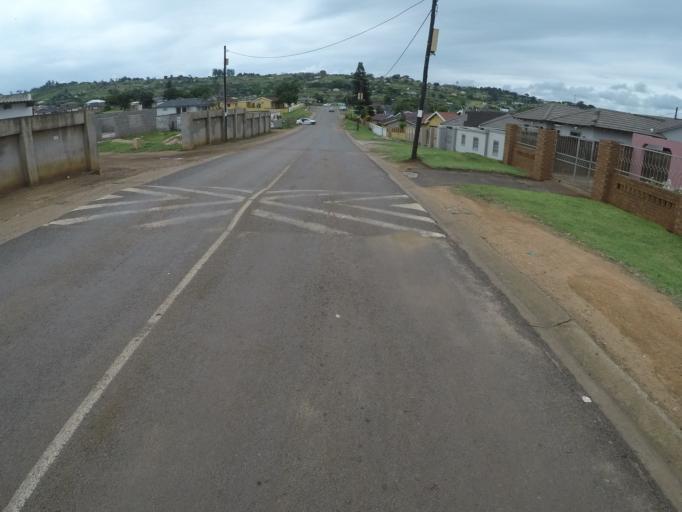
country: ZA
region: KwaZulu-Natal
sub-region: uThungulu District Municipality
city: Empangeni
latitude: -28.7753
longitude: 31.8481
